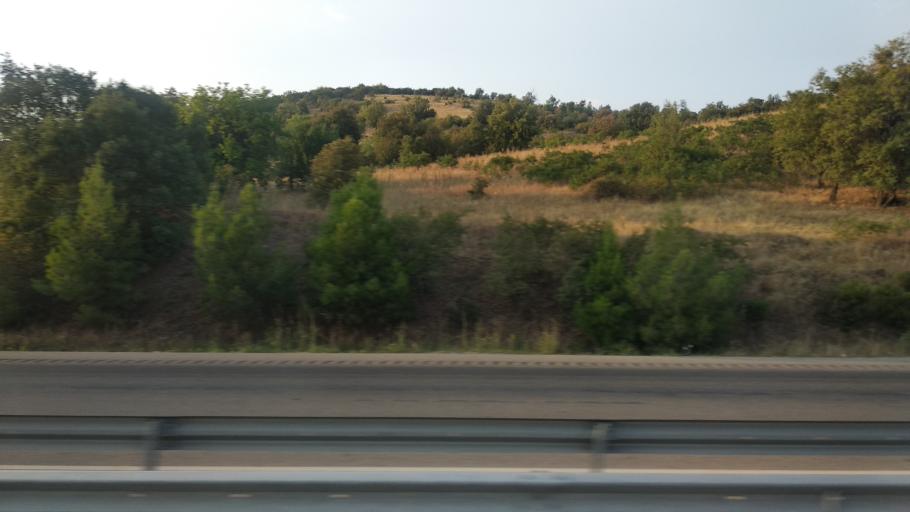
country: TR
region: Manisa
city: Menye
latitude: 38.5668
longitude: 28.5635
